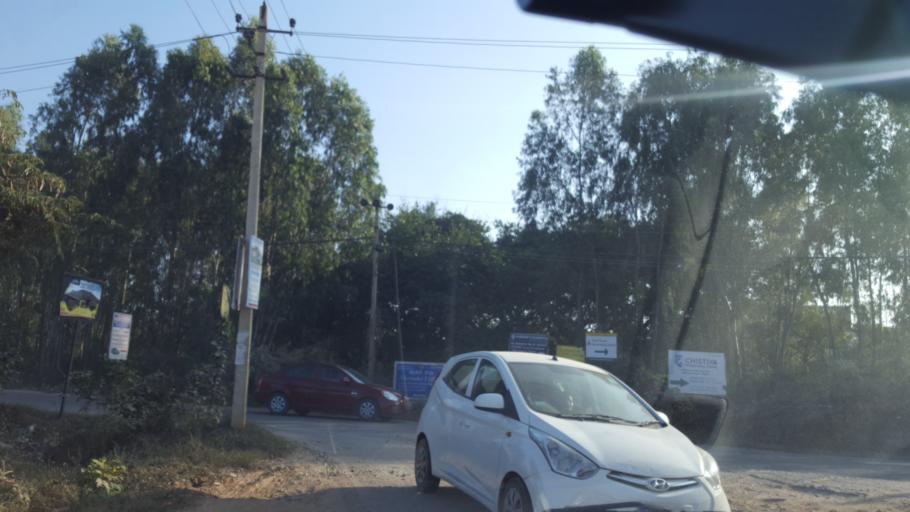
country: IN
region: Karnataka
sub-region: Bangalore Rural
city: Hoskote
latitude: 12.9184
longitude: 77.7572
